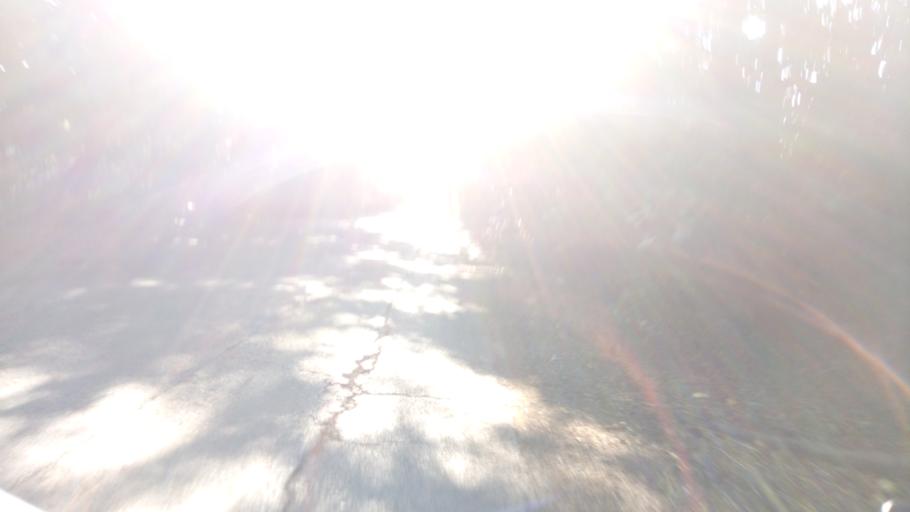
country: HU
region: Pest
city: Budaors
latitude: 47.4475
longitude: 18.9811
